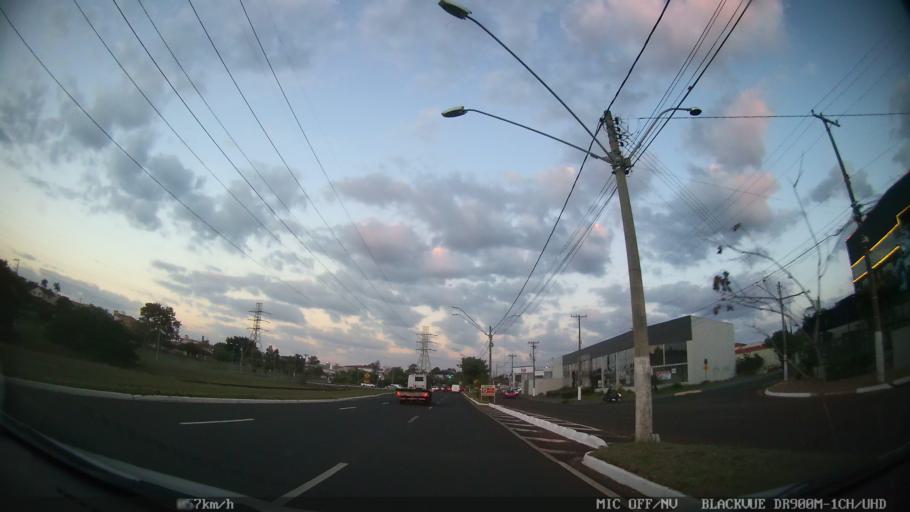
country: BR
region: Sao Paulo
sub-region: Ribeirao Preto
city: Ribeirao Preto
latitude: -21.2113
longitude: -47.7776
